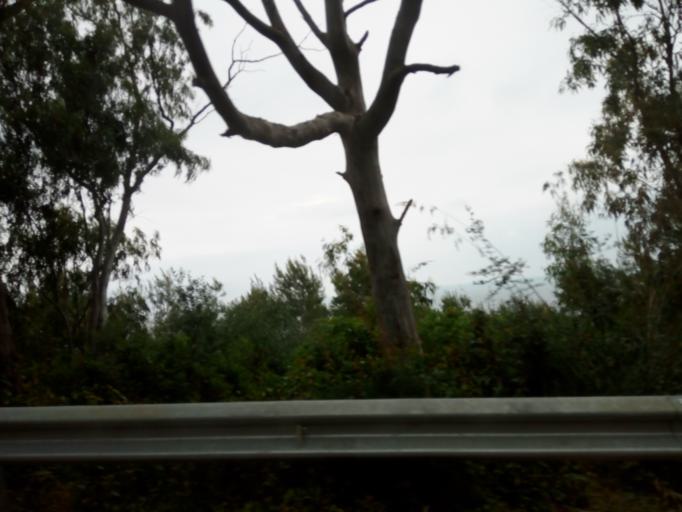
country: DZ
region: Tipaza
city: Tipasa
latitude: 36.5895
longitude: 2.5552
